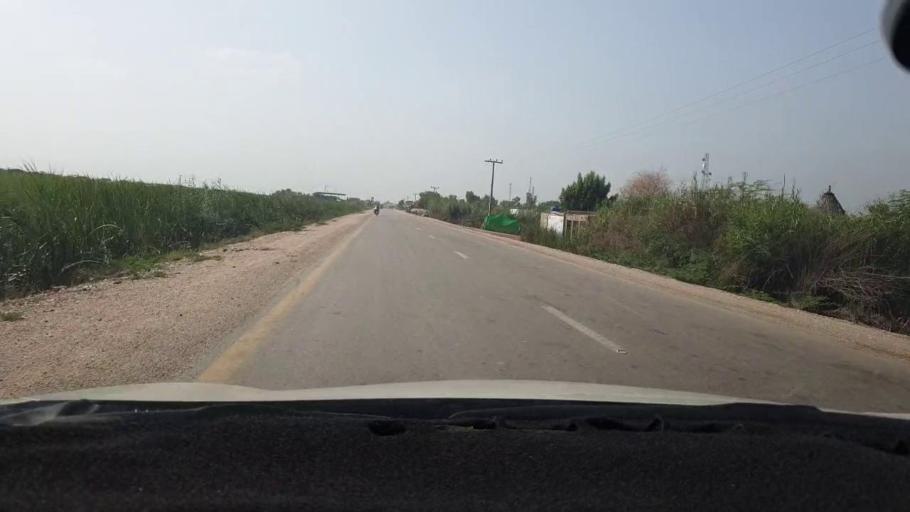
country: PK
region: Sindh
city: Tando Mittha Khan
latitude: 25.8048
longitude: 69.0723
